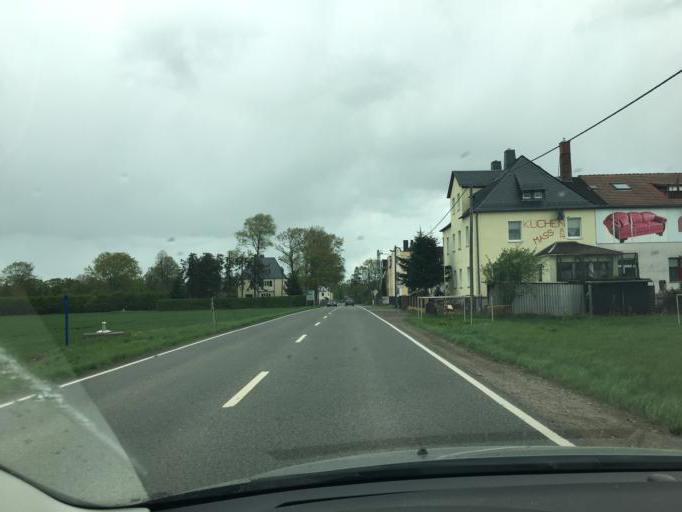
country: DE
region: Saxony
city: Limbach-Oberfrohna
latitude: 50.8449
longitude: 12.7713
